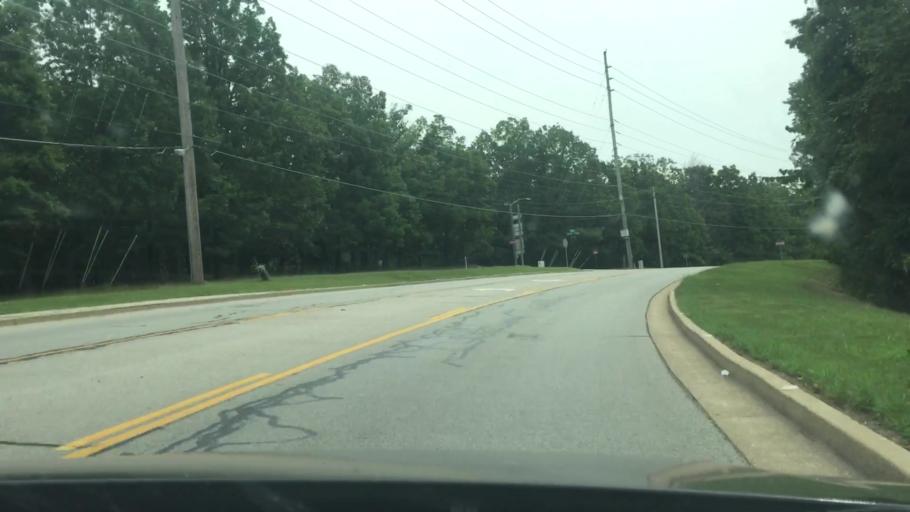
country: US
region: Missouri
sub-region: Miller County
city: Lake Ozark
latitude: 38.1954
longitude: -92.6747
